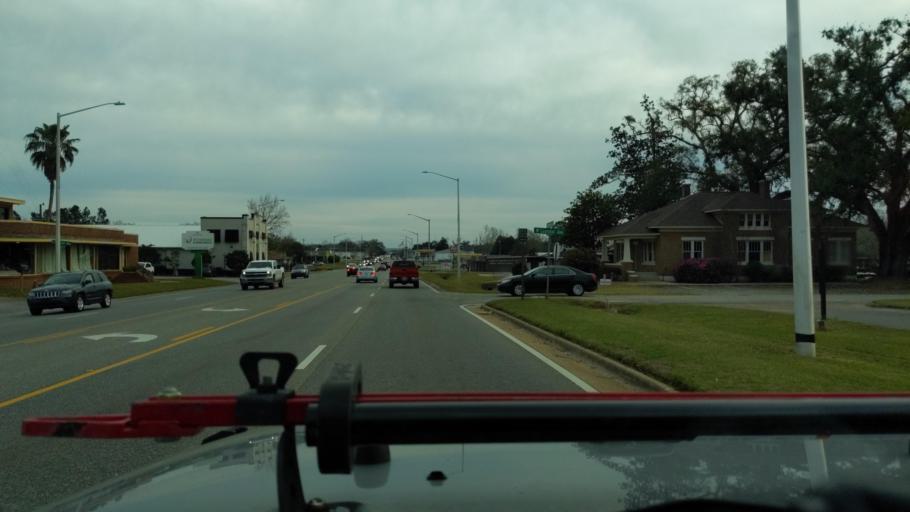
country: US
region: Alabama
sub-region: Baldwin County
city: Foley
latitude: 30.4155
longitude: -87.6838
